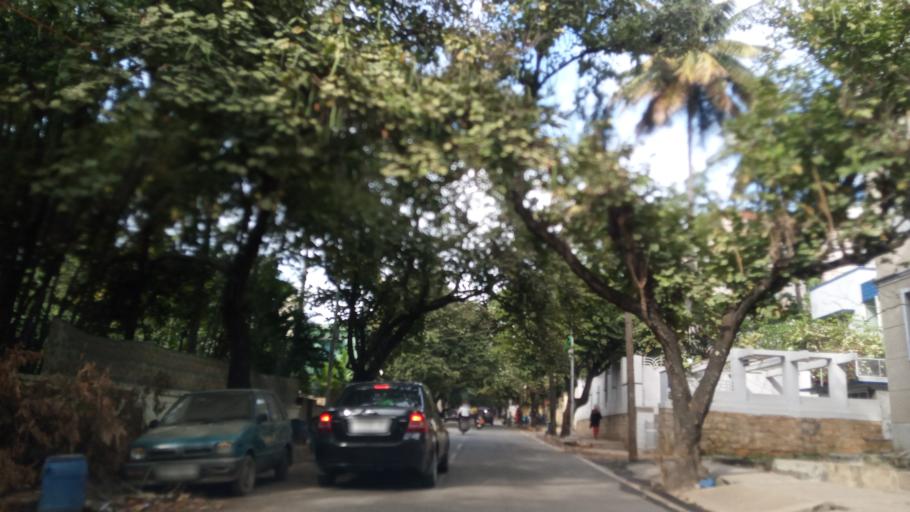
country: IN
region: Karnataka
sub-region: Bangalore Urban
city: Bangalore
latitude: 13.0075
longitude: 77.5664
